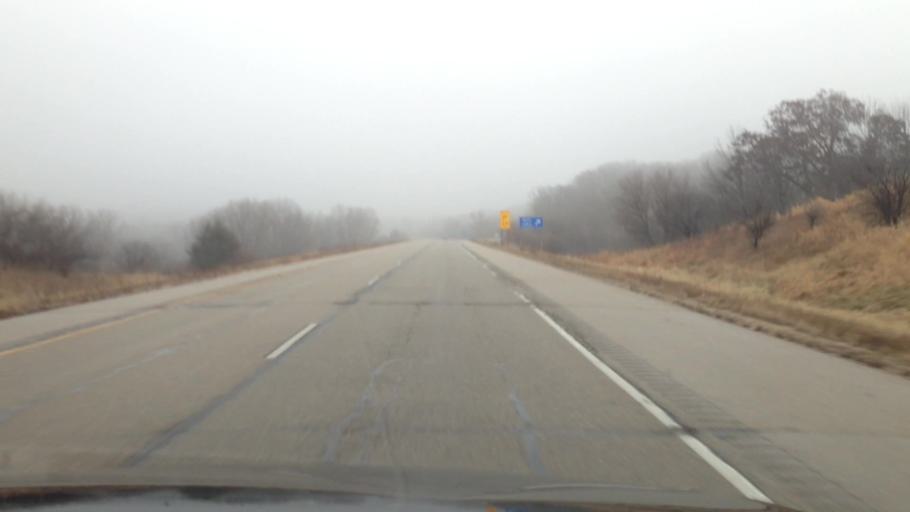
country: US
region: Wisconsin
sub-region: Walworth County
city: Elkhorn
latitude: 42.7184
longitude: -88.4703
